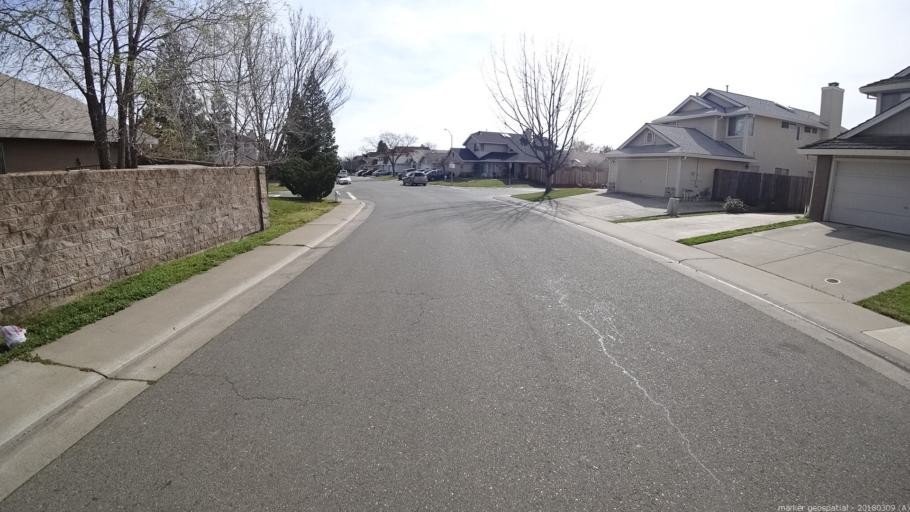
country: US
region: California
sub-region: Sacramento County
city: Laguna
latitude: 38.4540
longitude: -121.3945
